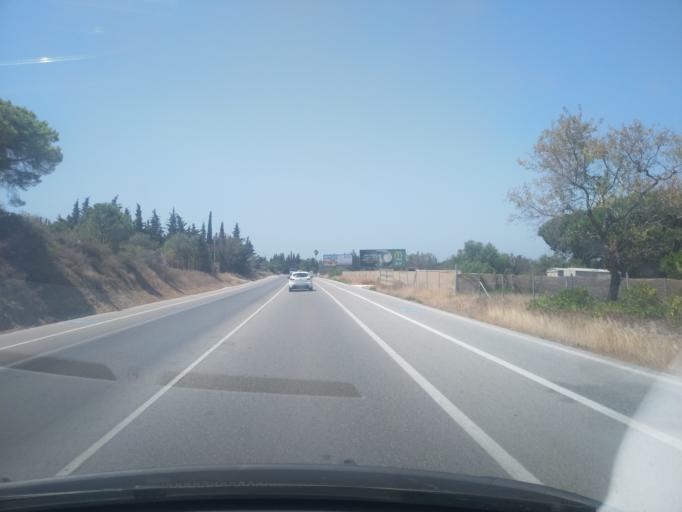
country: ES
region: Andalusia
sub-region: Provincia de Cadiz
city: Chiclana de la Frontera
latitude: 36.3899
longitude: -6.1408
